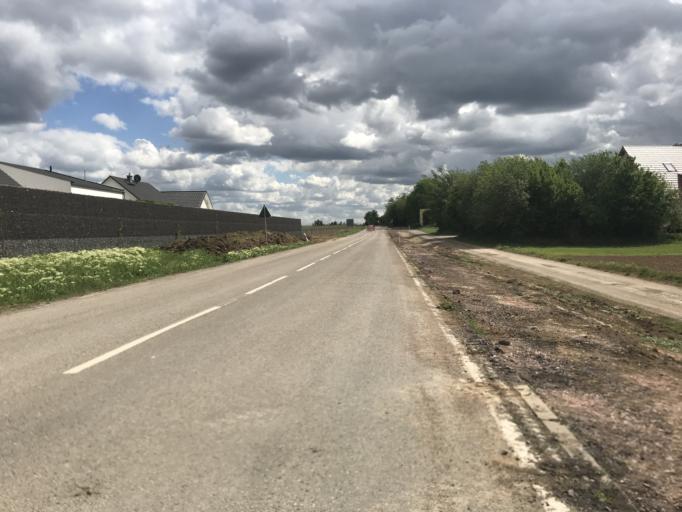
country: DE
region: Rheinland-Pfalz
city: Gau-Bischofsheim
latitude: 49.9123
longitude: 8.2688
